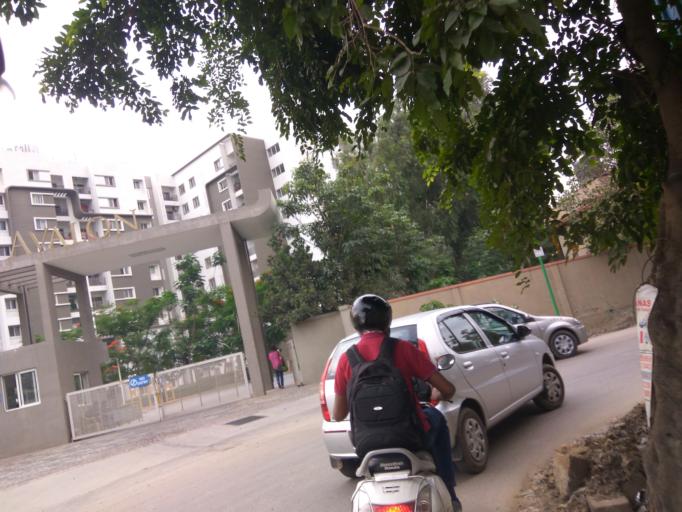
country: IN
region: Karnataka
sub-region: Bangalore Urban
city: Bangalore
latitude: 12.9752
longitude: 77.7069
